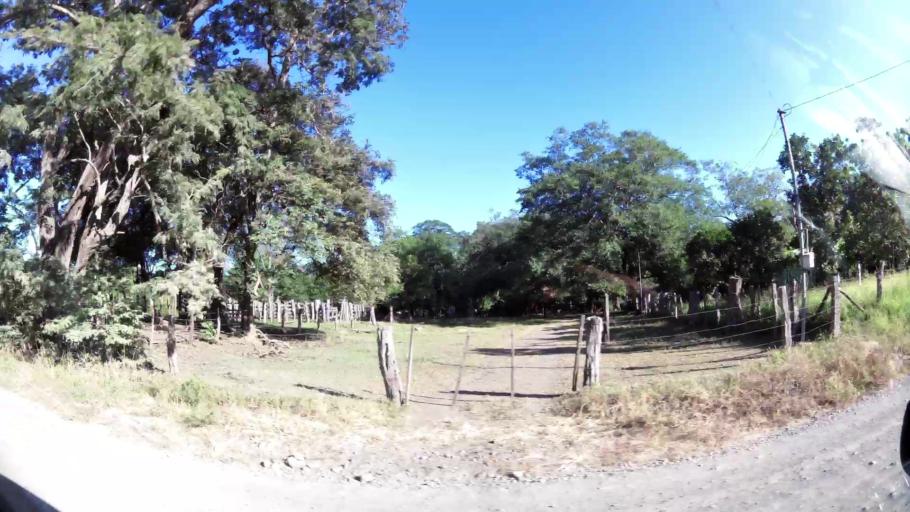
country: CR
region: Guanacaste
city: Sardinal
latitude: 10.4805
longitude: -85.6087
